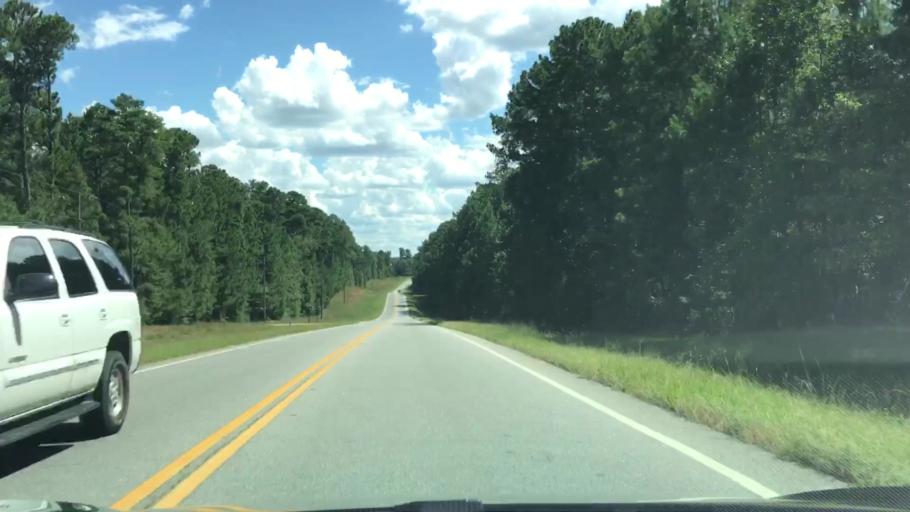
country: US
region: Georgia
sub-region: Greene County
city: Greensboro
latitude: 33.6595
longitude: -83.2412
